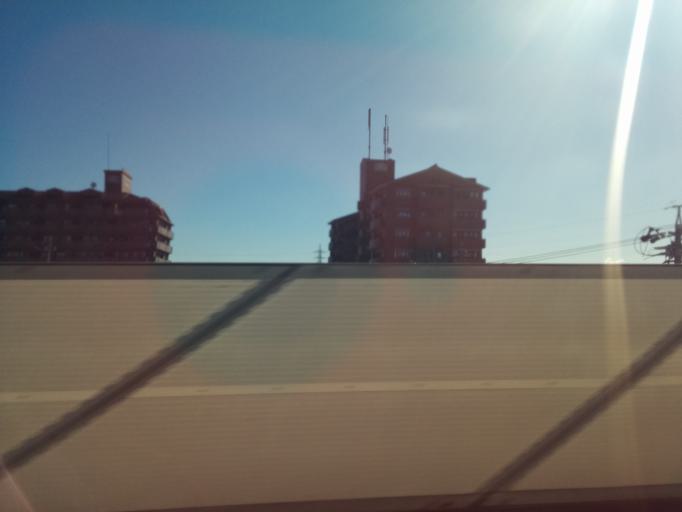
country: JP
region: Aichi
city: Anjo
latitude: 34.9596
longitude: 137.0691
